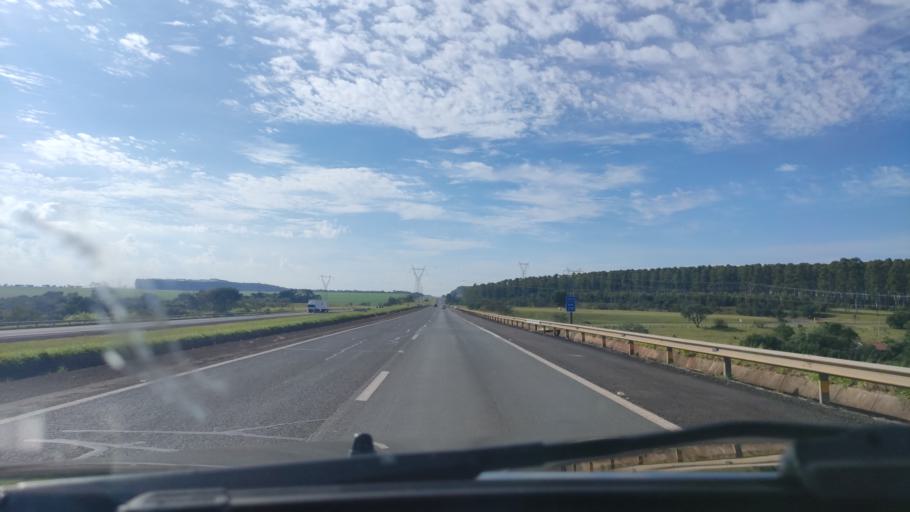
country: BR
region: Sao Paulo
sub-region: Itatinga
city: Itatinga
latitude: -23.0089
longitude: -48.7095
